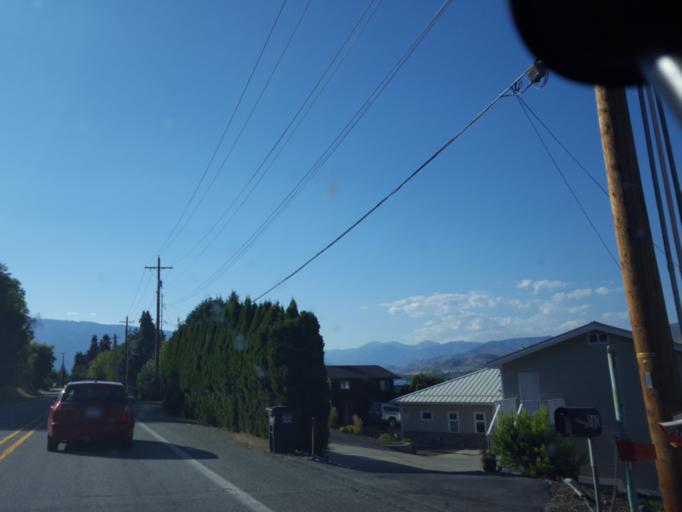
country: US
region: Washington
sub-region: Chelan County
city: Manson
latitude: 47.8431
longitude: -120.1015
